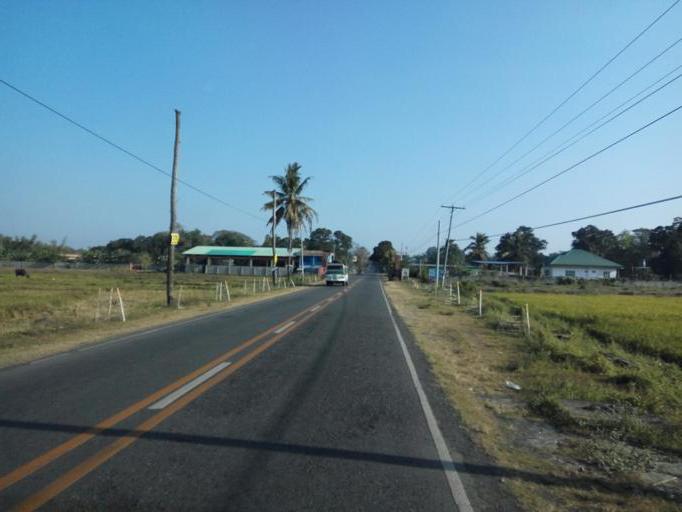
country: PH
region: Cagayan Valley
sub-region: Province of Cagayan
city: Iguig
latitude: 17.7414
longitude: 121.7380
